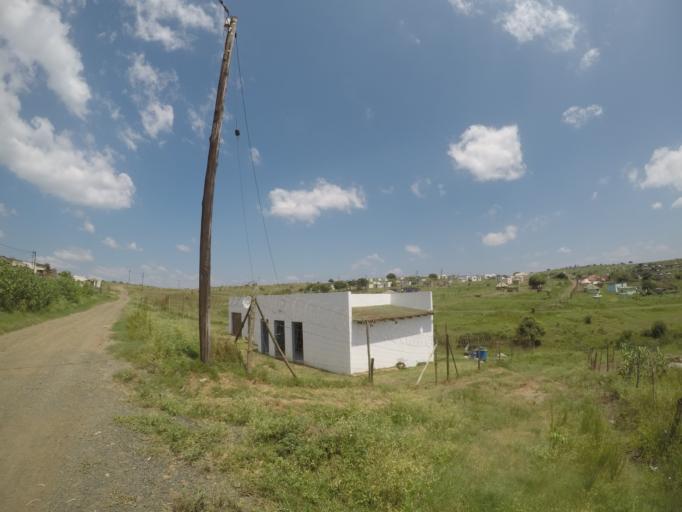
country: ZA
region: KwaZulu-Natal
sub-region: uThungulu District Municipality
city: Empangeni
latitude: -28.6065
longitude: 31.7408
